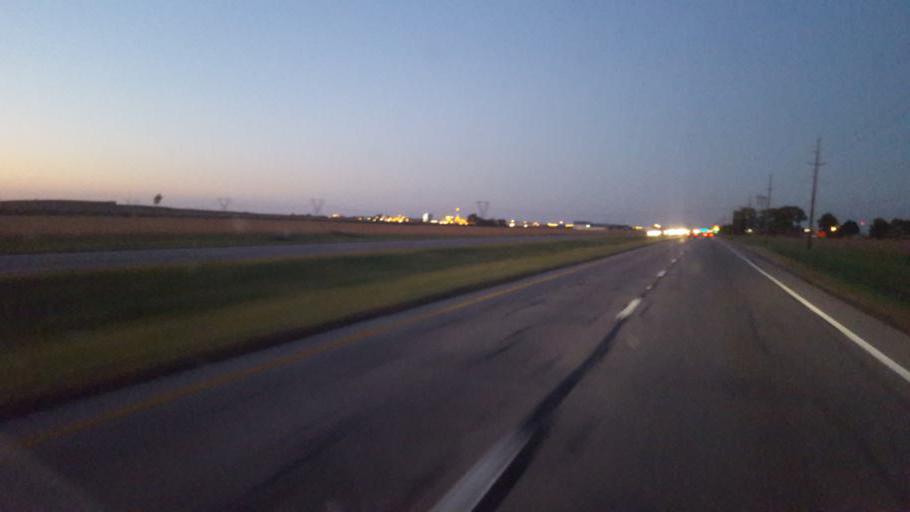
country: US
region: Ohio
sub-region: Pickaway County
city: Logan Elm Village
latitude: 39.5408
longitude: -82.9657
